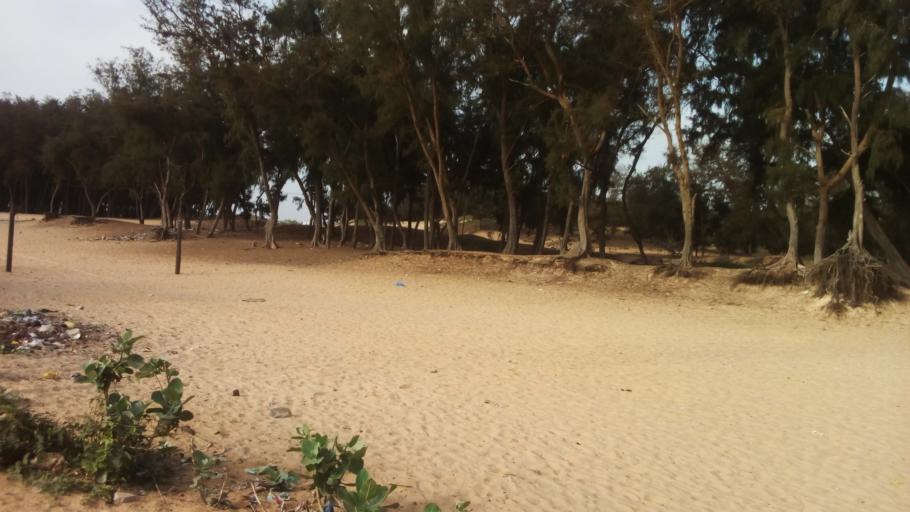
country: SN
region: Dakar
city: Pikine
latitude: 14.8005
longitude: -17.3410
